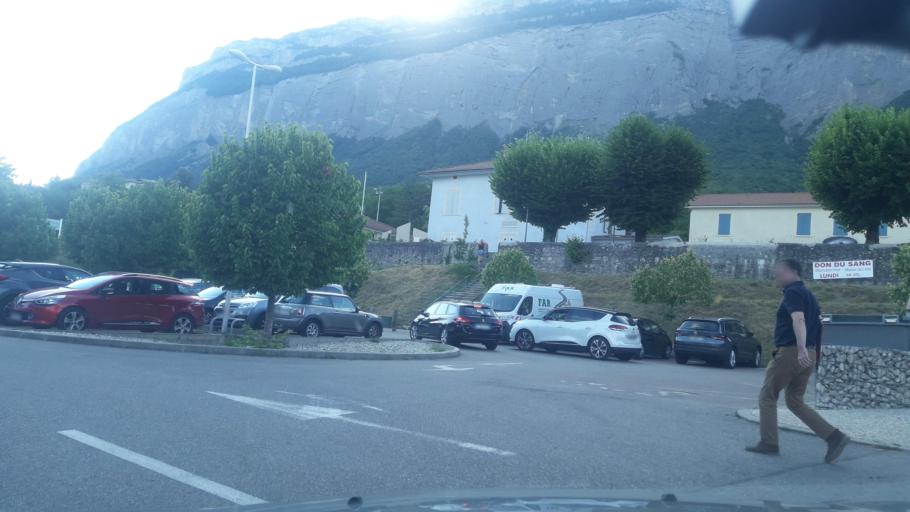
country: FR
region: Rhone-Alpes
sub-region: Departement de l'Isere
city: Biviers
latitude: 45.2379
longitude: 5.8035
